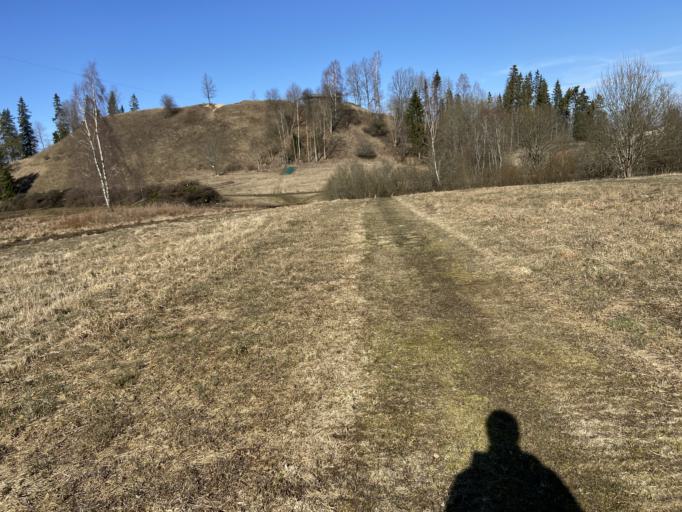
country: EE
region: Tartu
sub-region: Elva linn
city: Elva
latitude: 58.0559
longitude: 26.5069
